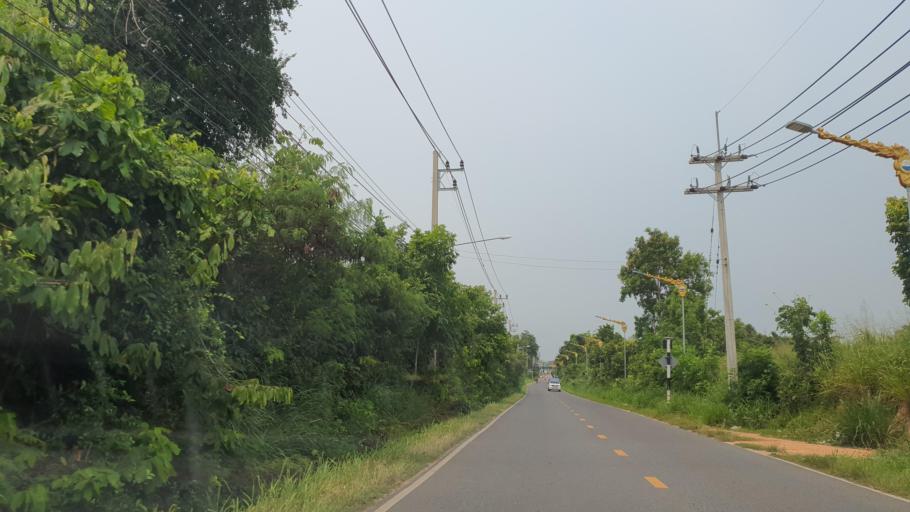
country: TH
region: Chon Buri
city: Phatthaya
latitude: 12.8978
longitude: 100.9147
